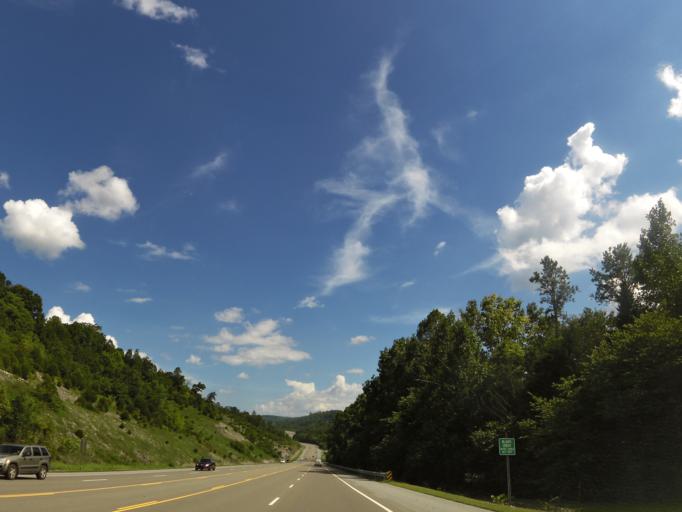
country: US
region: Tennessee
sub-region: Claiborne County
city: Harrogate
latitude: 36.5210
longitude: -83.6157
